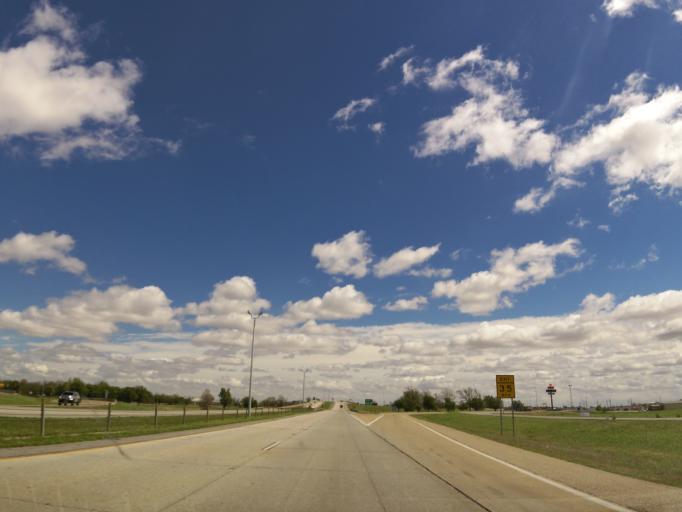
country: US
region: Arkansas
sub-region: Craighead County
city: Jonesboro
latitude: 35.8069
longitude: -90.6429
